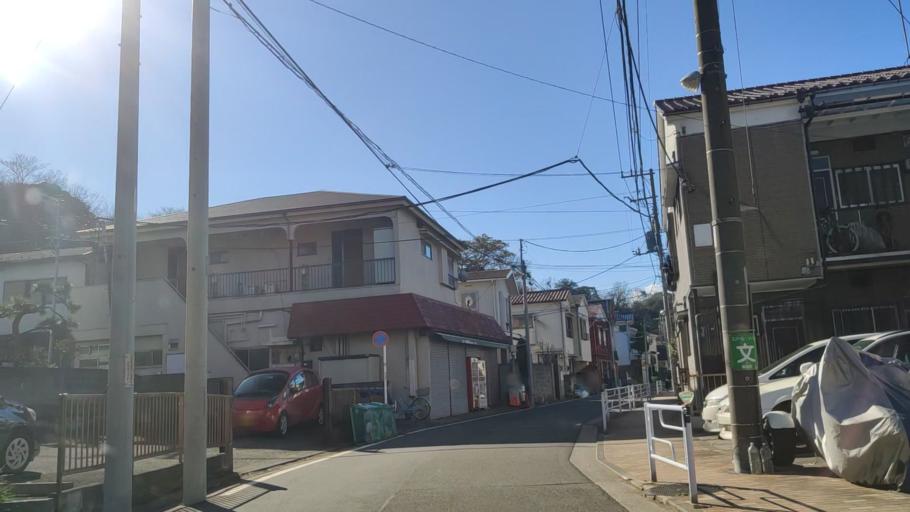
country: JP
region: Kanagawa
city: Yokohama
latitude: 35.4284
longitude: 139.6582
